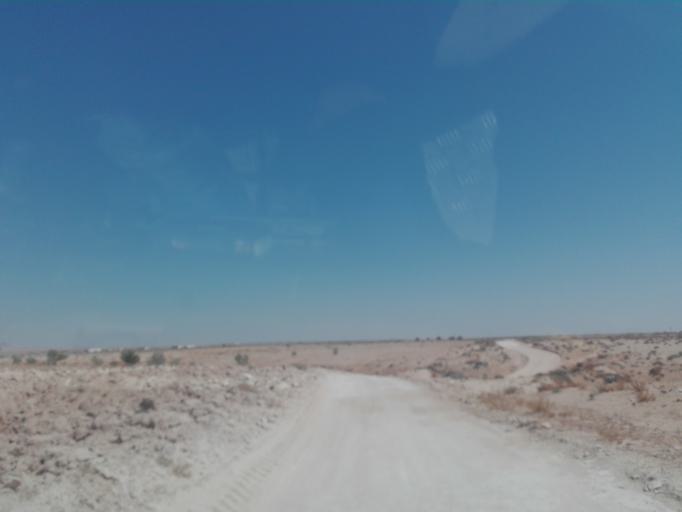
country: TN
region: Safaqis
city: Skhira
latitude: 34.3994
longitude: 9.9289
